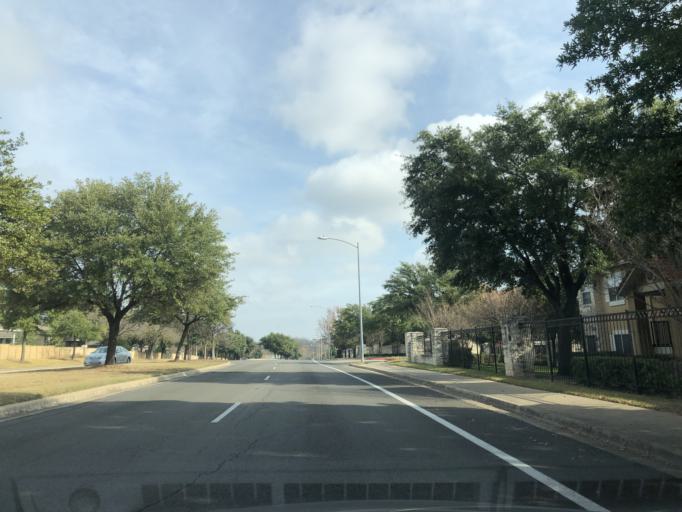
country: US
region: Texas
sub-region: Travis County
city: Wells Branch
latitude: 30.4236
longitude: -97.6808
